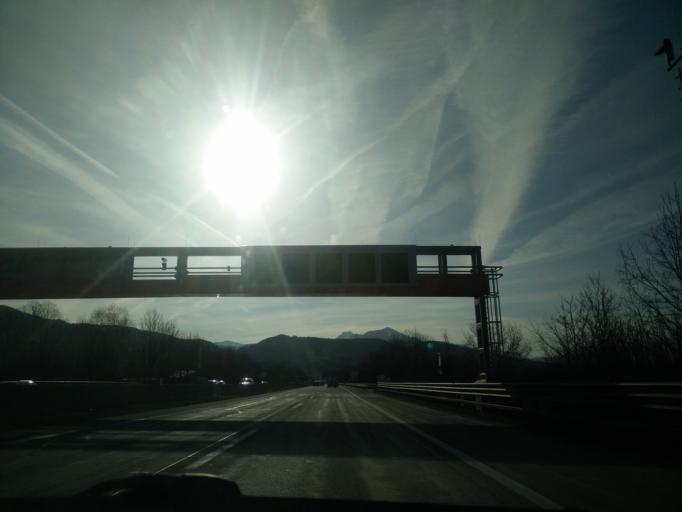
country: AT
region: Salzburg
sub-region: Politischer Bezirk Salzburg-Umgebung
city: Anif
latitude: 47.7366
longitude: 13.0634
